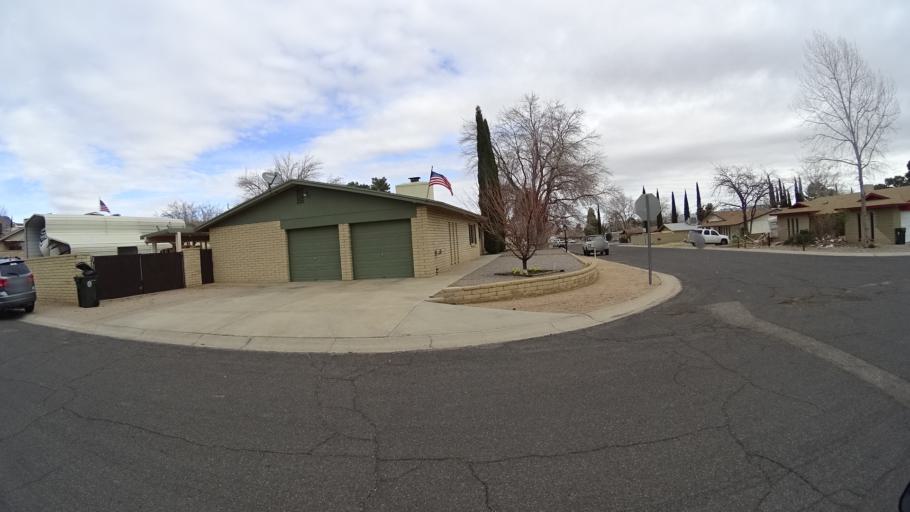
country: US
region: Arizona
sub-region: Mohave County
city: New Kingman-Butler
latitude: 35.2377
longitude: -114.0441
